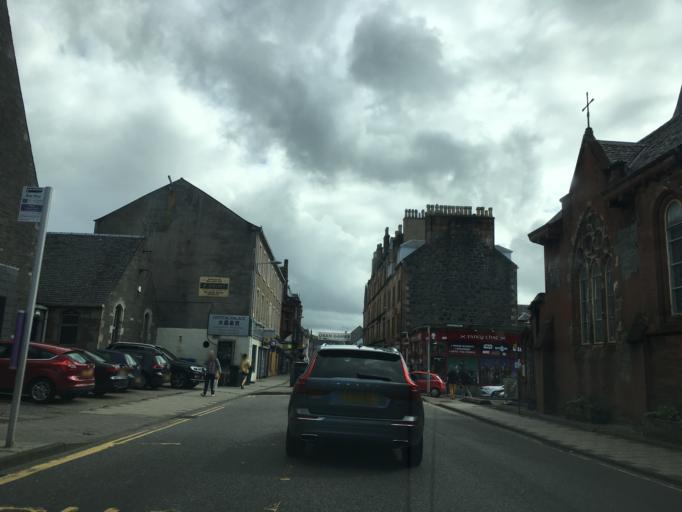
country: GB
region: Scotland
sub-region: Argyll and Bute
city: Oban
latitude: 56.4169
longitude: -5.4733
